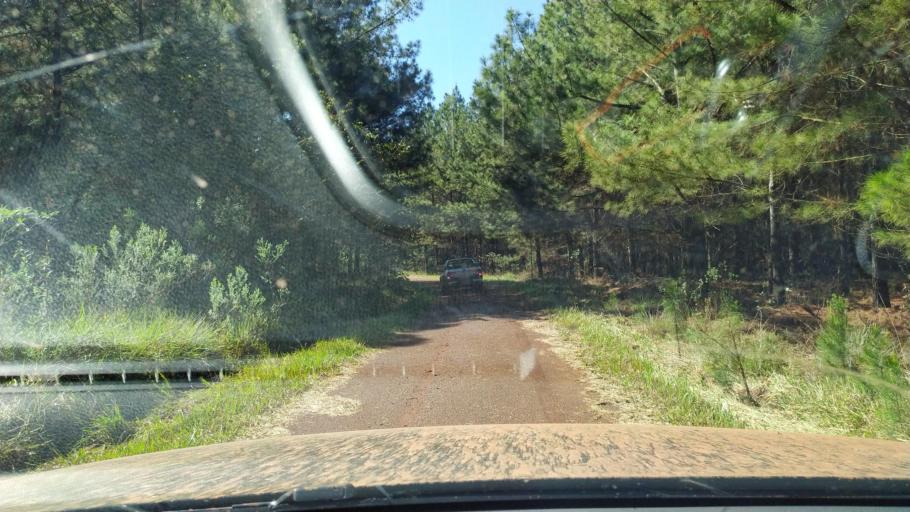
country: AR
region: Corrientes
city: Santo Tome
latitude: -28.3625
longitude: -56.0389
